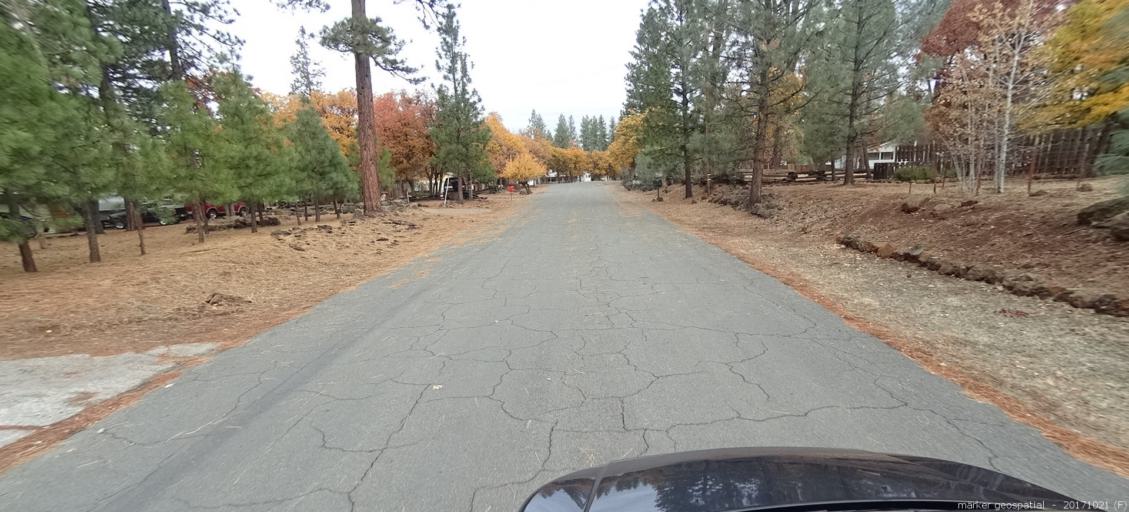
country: US
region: California
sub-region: Shasta County
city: Burney
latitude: 40.9169
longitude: -121.5578
